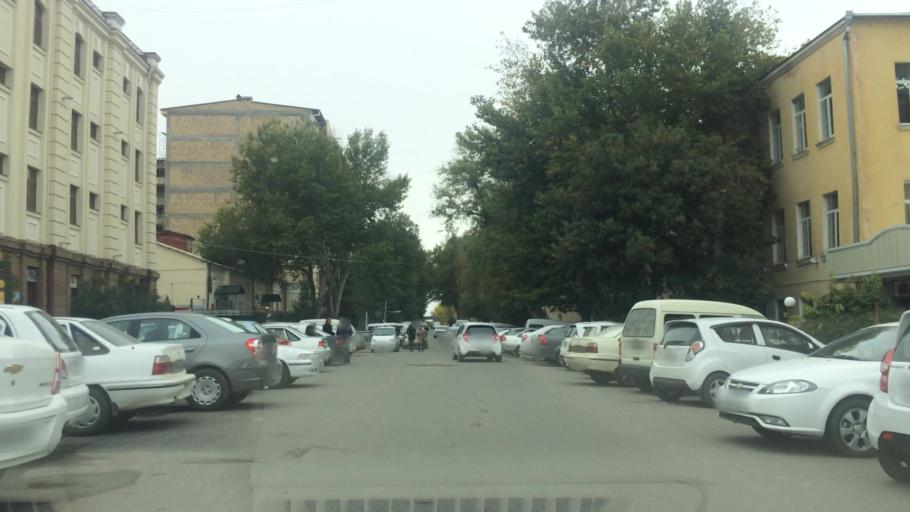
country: UZ
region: Samarqand
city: Samarqand
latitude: 39.6522
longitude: 66.9619
